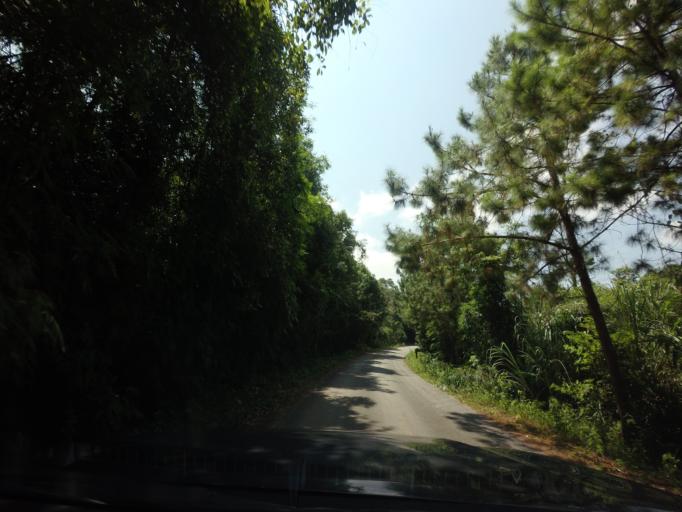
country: TH
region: Loei
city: Na Haeo
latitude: 17.5001
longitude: 100.9391
